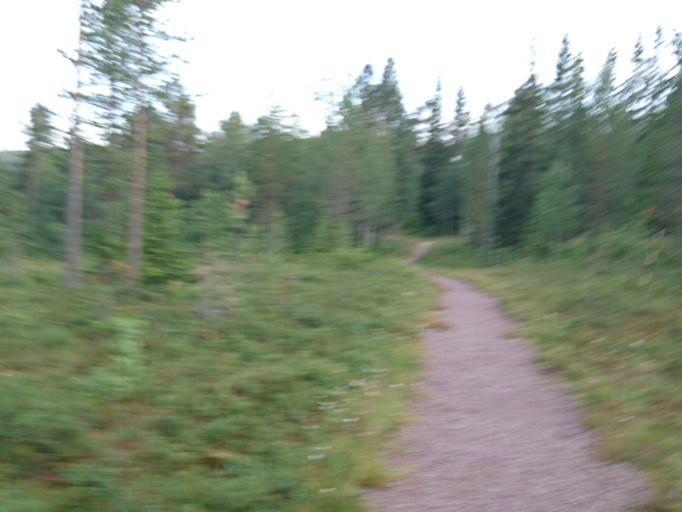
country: SE
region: Dalarna
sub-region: Malung-Saelens kommun
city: Malung
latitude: 61.1733
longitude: 13.1761
